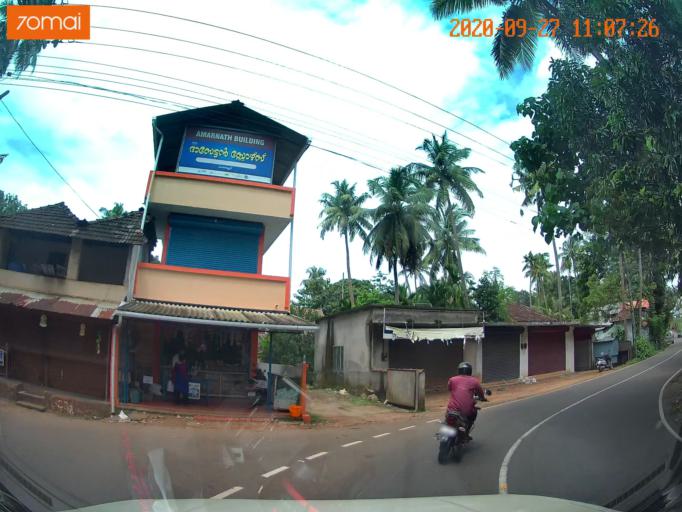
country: IN
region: Kerala
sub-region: Thrissur District
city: Irinjalakuda
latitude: 10.4279
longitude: 76.2366
